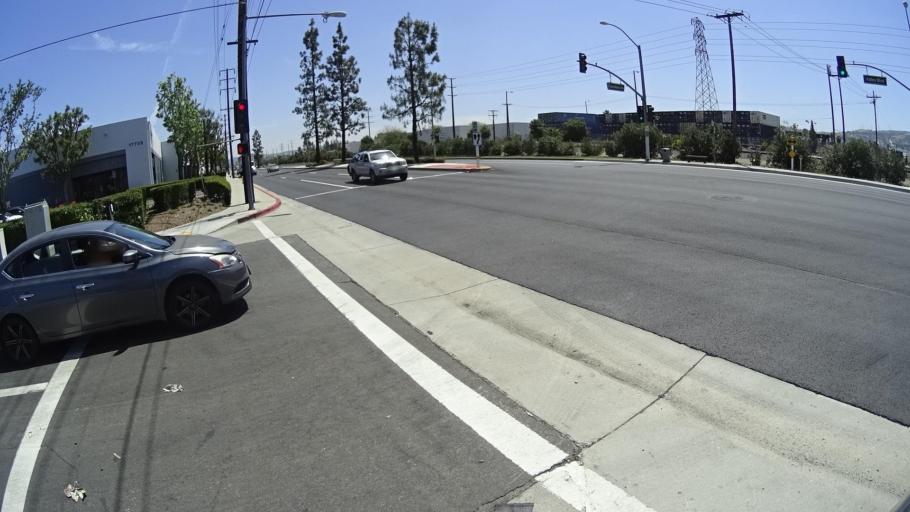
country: US
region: California
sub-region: Los Angeles County
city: South San Jose Hills
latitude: 34.0080
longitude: -117.9171
